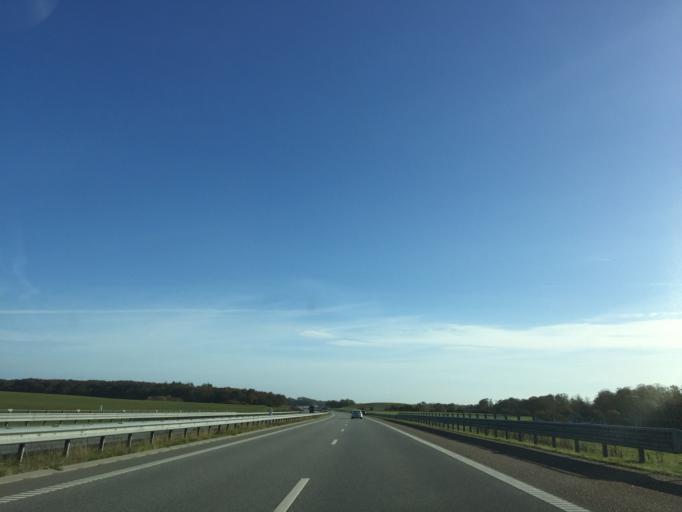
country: DK
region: South Denmark
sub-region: Sonderborg Kommune
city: Grasten
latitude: 54.9588
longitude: 9.5708
